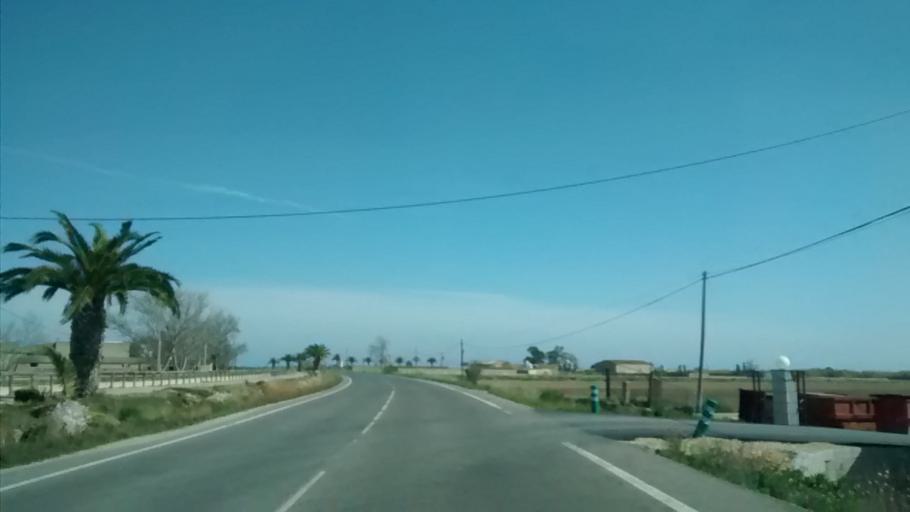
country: ES
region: Catalonia
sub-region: Provincia de Tarragona
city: Deltebre
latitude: 40.7089
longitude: 0.7602
